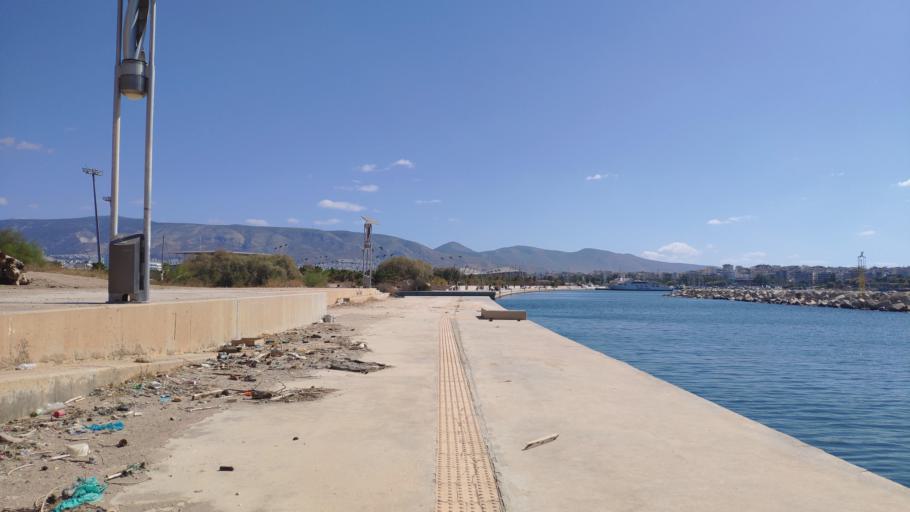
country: GR
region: Attica
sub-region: Nomarchia Athinas
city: Moskhaton
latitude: 37.9402
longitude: 23.6798
